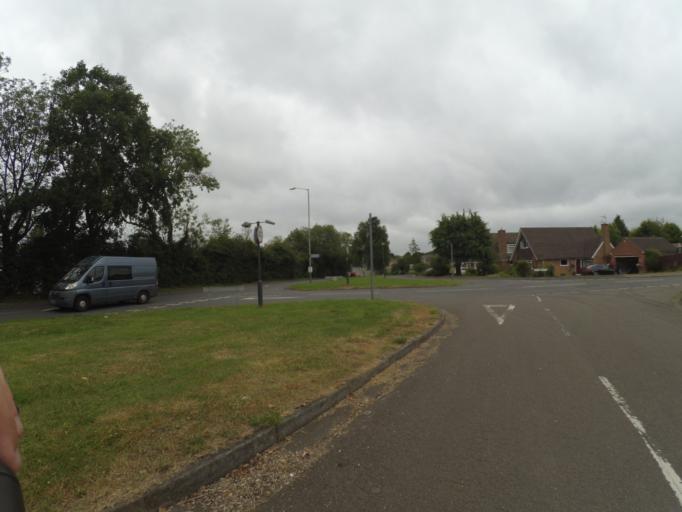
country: GB
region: England
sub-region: Warwickshire
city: Rugby
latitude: 52.3530
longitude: -1.2725
